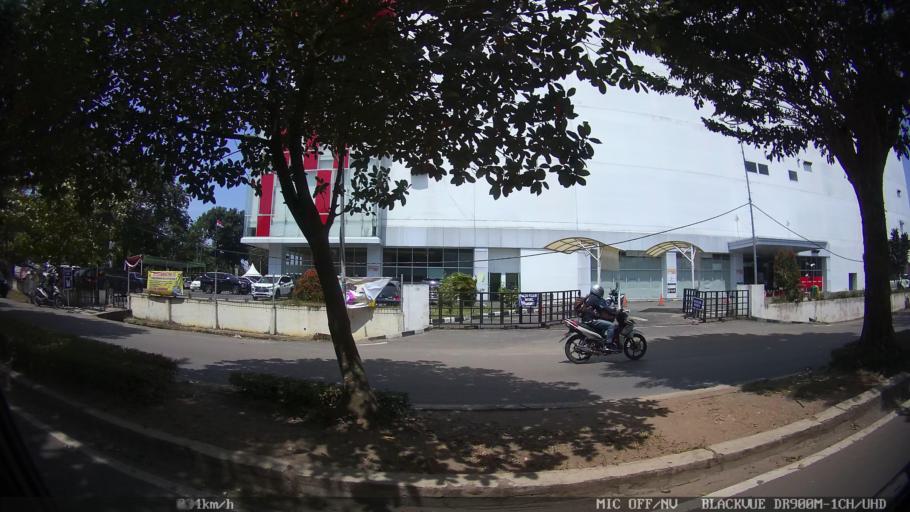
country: ID
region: Lampung
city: Kedaton
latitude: -5.3836
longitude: 105.2817
